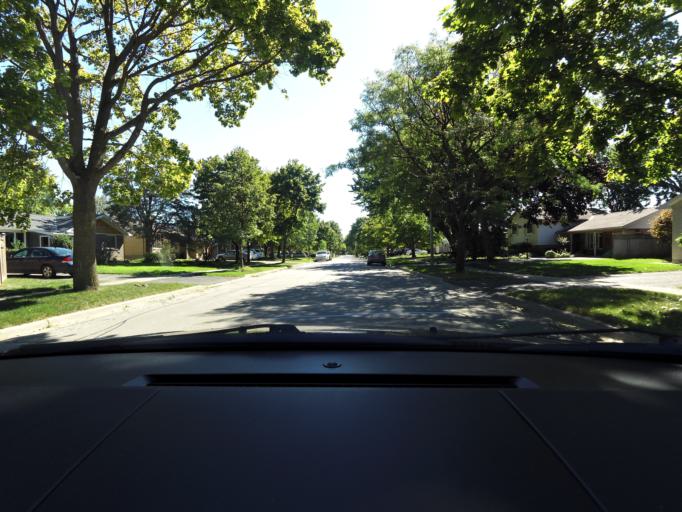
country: CA
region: Ontario
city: Burlington
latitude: 43.3550
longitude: -79.8154
